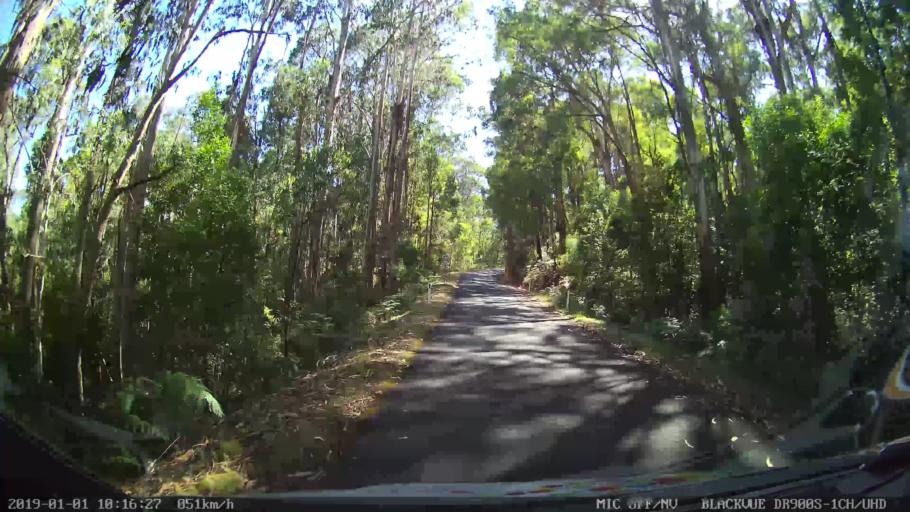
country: AU
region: New South Wales
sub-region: Snowy River
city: Jindabyne
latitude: -36.0939
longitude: 148.1674
